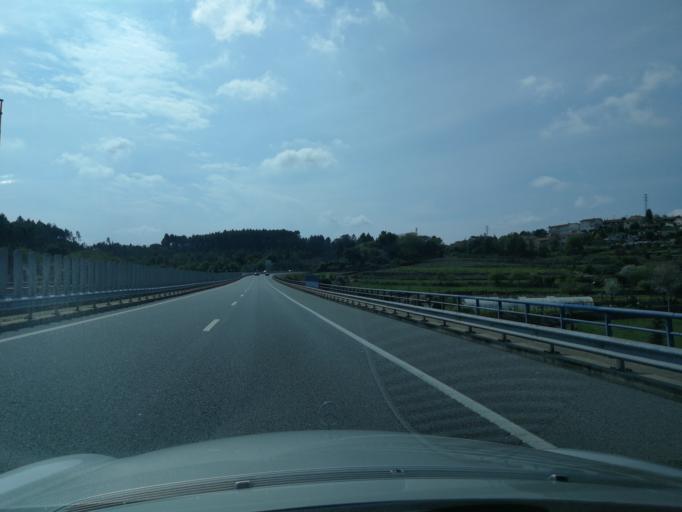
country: PT
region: Braga
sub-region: Vila Nova de Famalicao
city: Calendario
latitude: 41.3834
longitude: -8.5236
